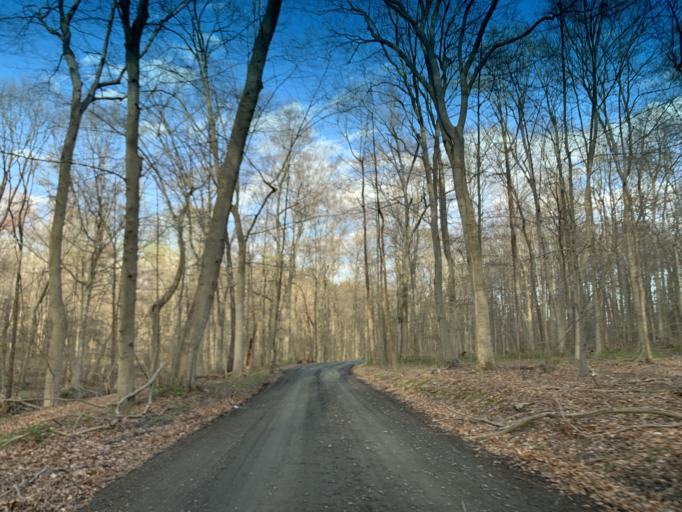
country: US
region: Maryland
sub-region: Harford County
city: South Bel Air
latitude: 39.5967
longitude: -76.3011
